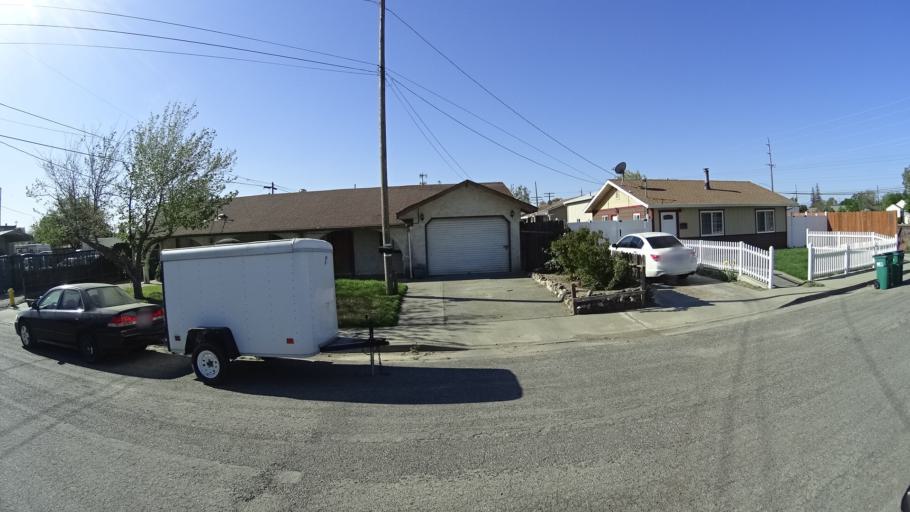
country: US
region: California
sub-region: Glenn County
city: Orland
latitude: 39.7532
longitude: -122.1963
